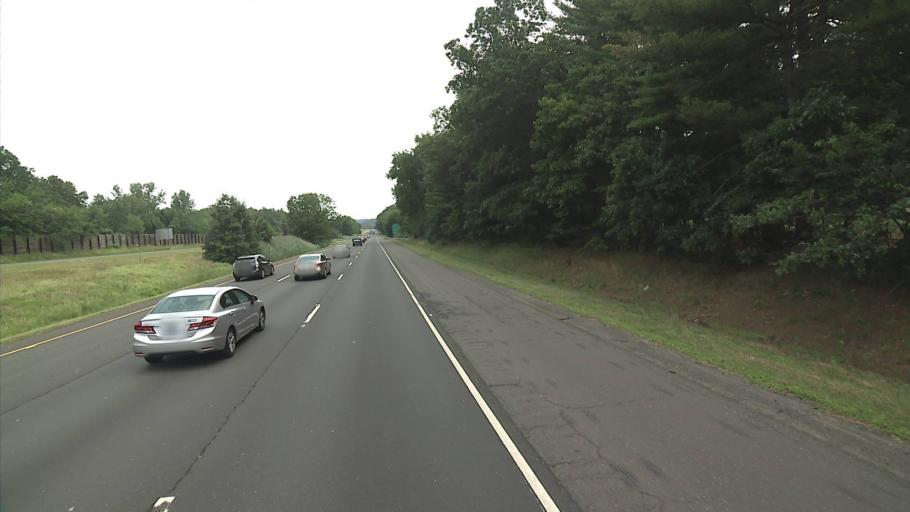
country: US
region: Connecticut
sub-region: Hartford County
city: Plainville
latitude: 41.6444
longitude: -72.8616
